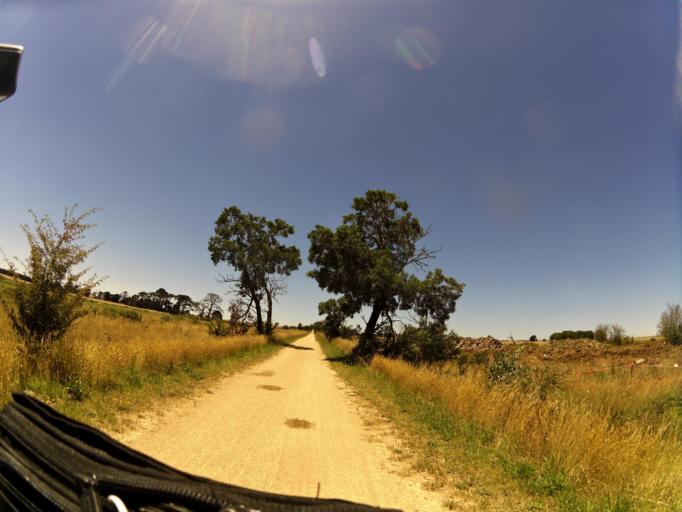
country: AU
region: Victoria
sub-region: Ballarat North
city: Newington
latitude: -37.5503
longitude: 143.7568
